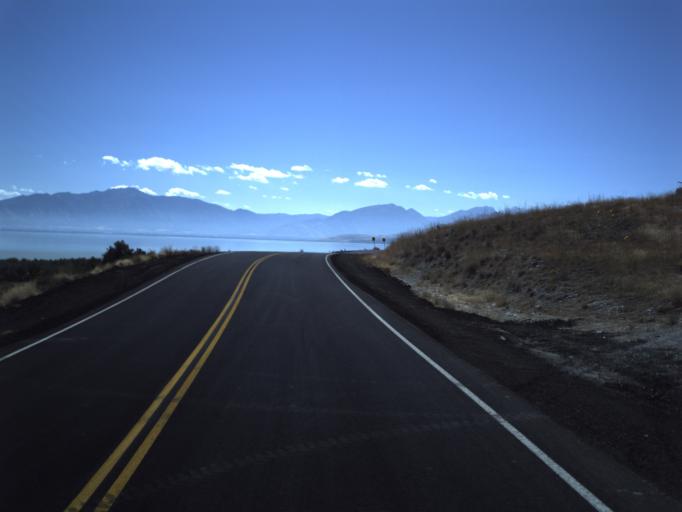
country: US
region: Utah
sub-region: Utah County
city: Saratoga Springs
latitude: 40.2528
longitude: -111.8670
